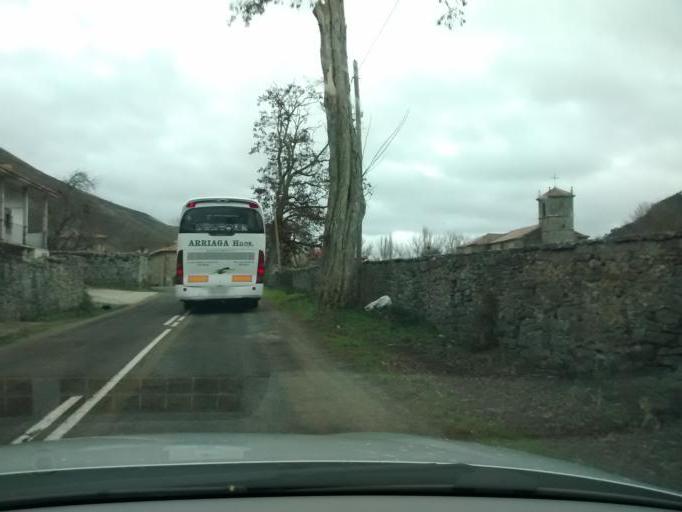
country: ES
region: Castille and Leon
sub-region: Provincia de Burgos
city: Espinosa de los Monteros
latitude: 43.0983
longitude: -3.5667
